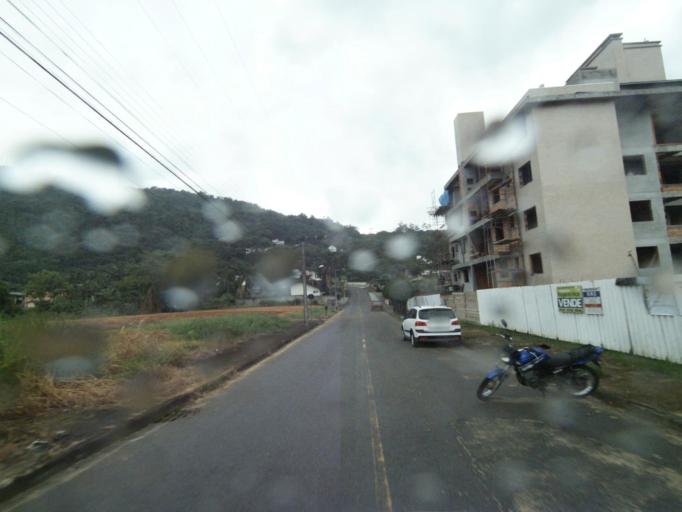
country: BR
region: Santa Catarina
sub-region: Pomerode
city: Pomerode
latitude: -26.7336
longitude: -49.1794
